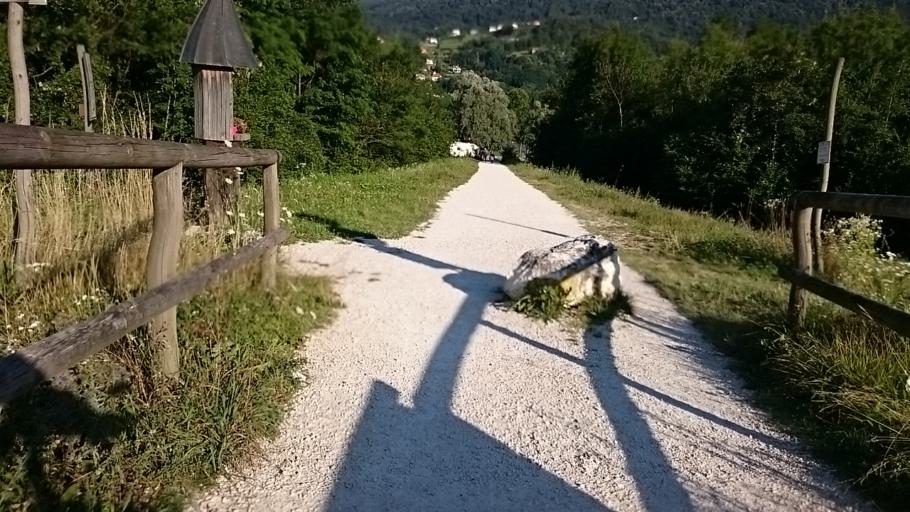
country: IT
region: Veneto
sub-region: Provincia di Belluno
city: Farra d'Alpago
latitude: 46.1201
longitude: 12.3491
